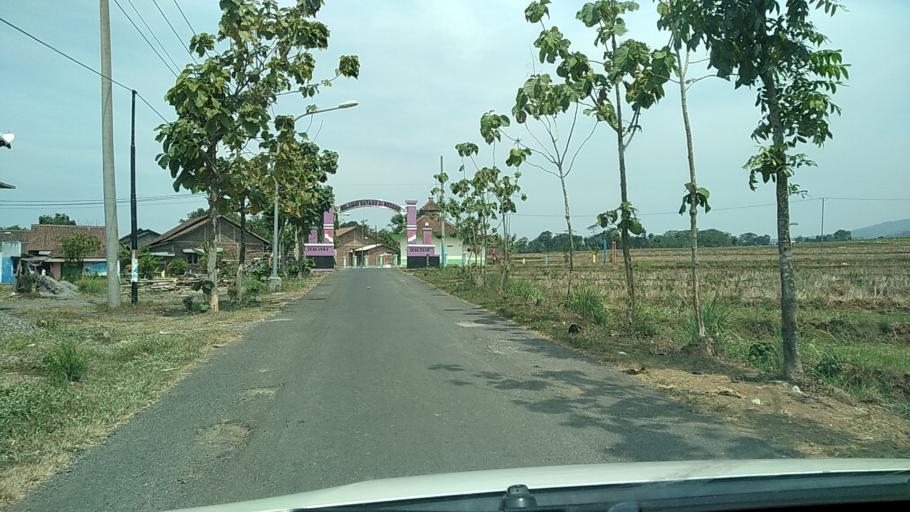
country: ID
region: Central Java
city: Ungaran
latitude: -7.0799
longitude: 110.3264
